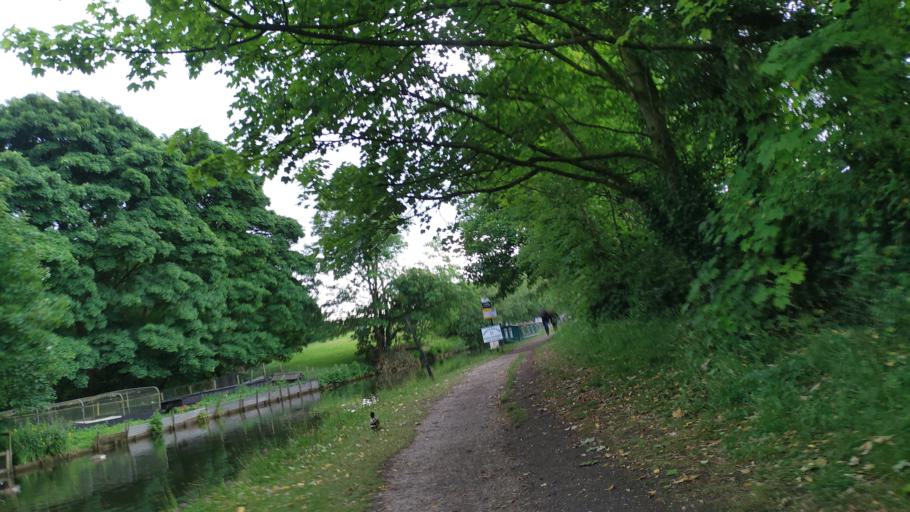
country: GB
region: England
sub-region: Lancashire
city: Chorley
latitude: 53.6894
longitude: -2.6058
